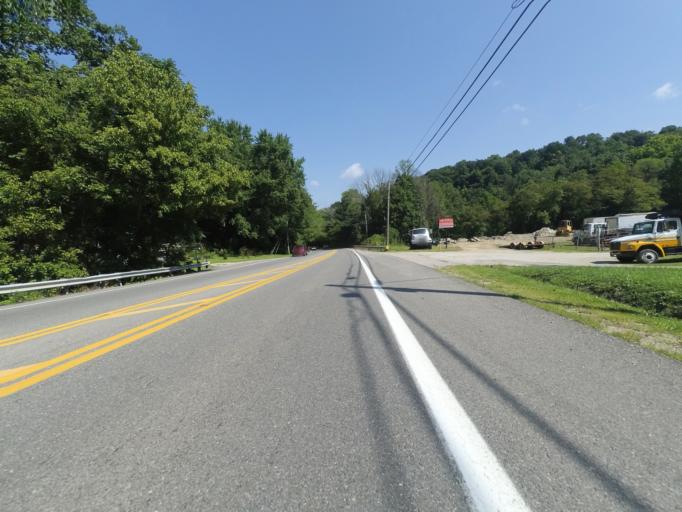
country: US
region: West Virginia
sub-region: Wayne County
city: Lavalette
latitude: 38.3654
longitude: -82.4537
